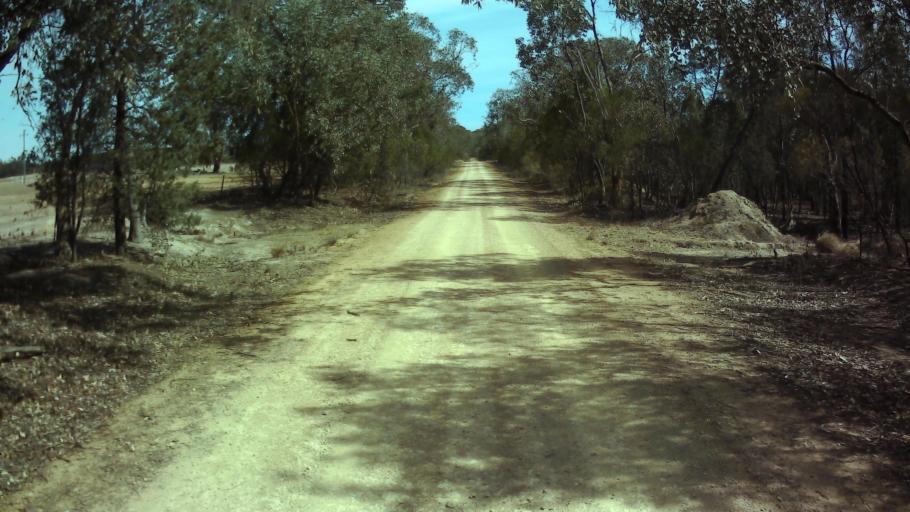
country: AU
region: New South Wales
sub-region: Weddin
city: Grenfell
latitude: -33.8748
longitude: 148.1487
